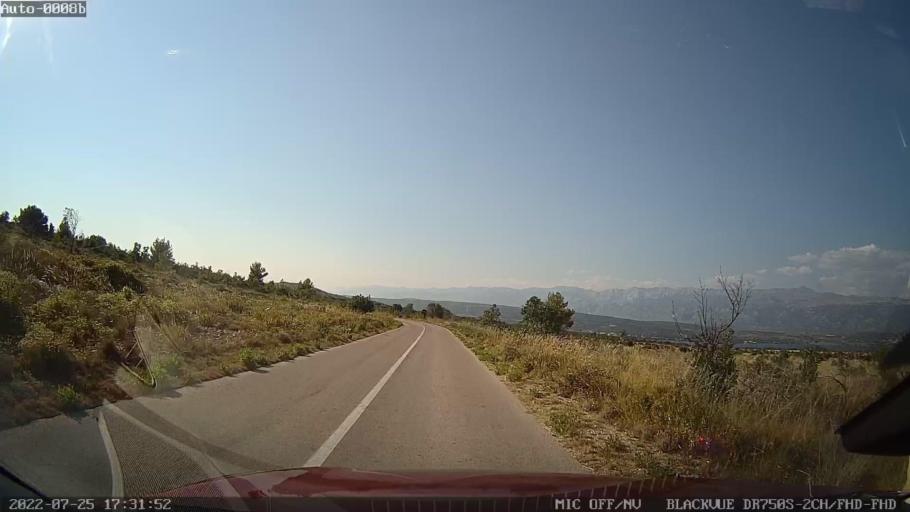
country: HR
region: Zadarska
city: Posedarje
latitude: 44.1728
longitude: 15.4969
